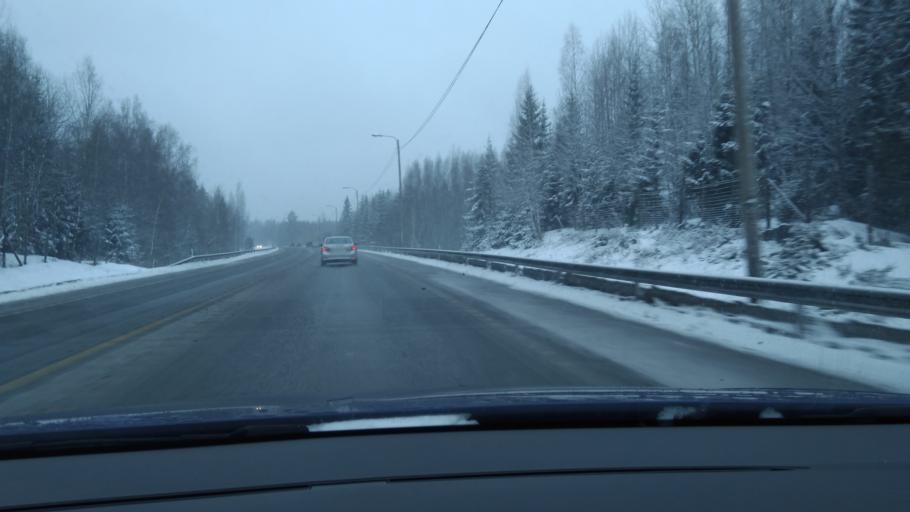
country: FI
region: Pirkanmaa
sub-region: Tampere
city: Tampere
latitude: 61.5191
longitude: 23.9205
